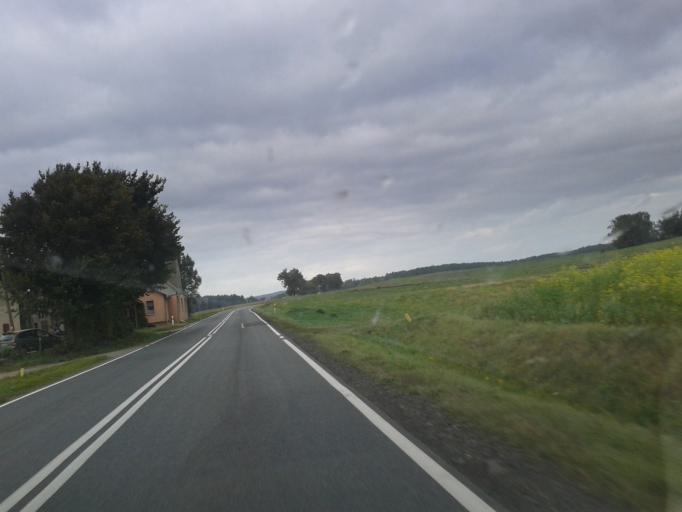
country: PL
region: Kujawsko-Pomorskie
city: Kamien Krajenski
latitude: 53.5033
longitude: 17.5075
